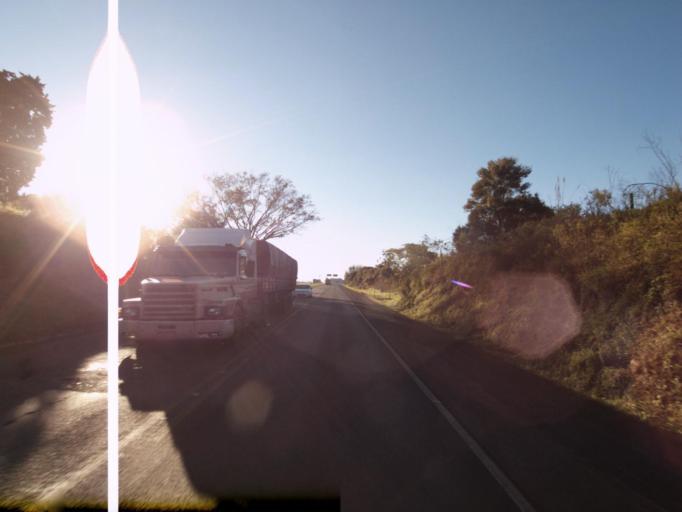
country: BR
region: Santa Catarina
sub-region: Chapeco
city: Chapeco
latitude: -26.9005
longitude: -52.9153
